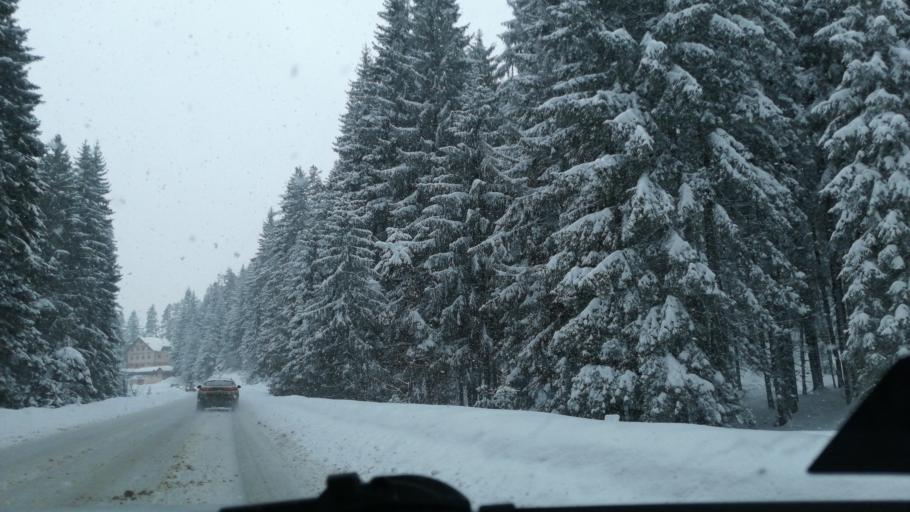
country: BA
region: Republika Srpska
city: Pale
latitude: 43.9237
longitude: 18.6535
